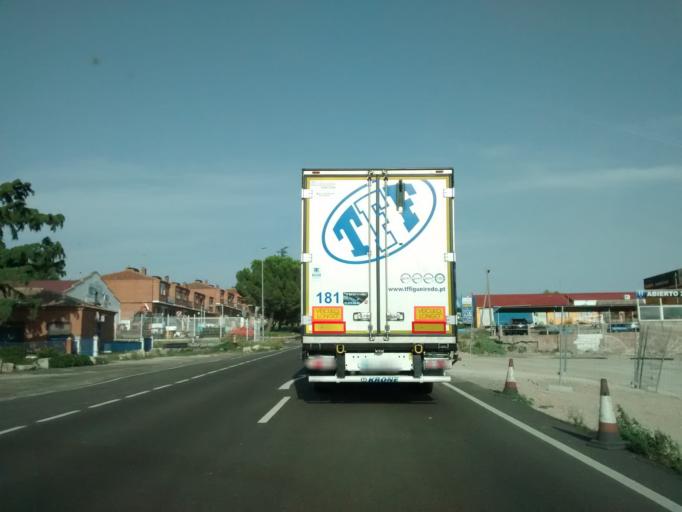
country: ES
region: Aragon
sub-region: Provincia de Zaragoza
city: Borja
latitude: 41.8318
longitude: -1.5201
